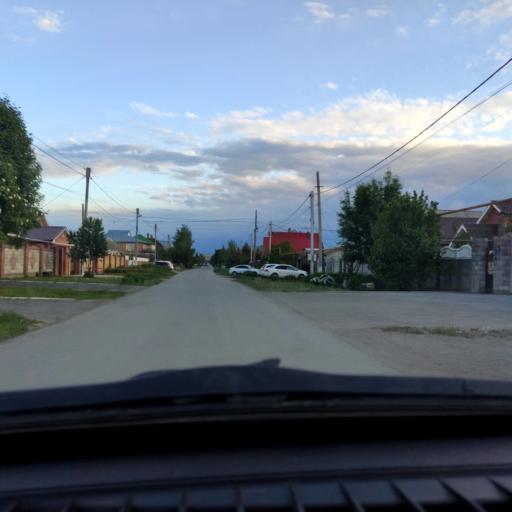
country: RU
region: Samara
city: Tol'yatti
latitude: 53.5632
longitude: 49.4030
